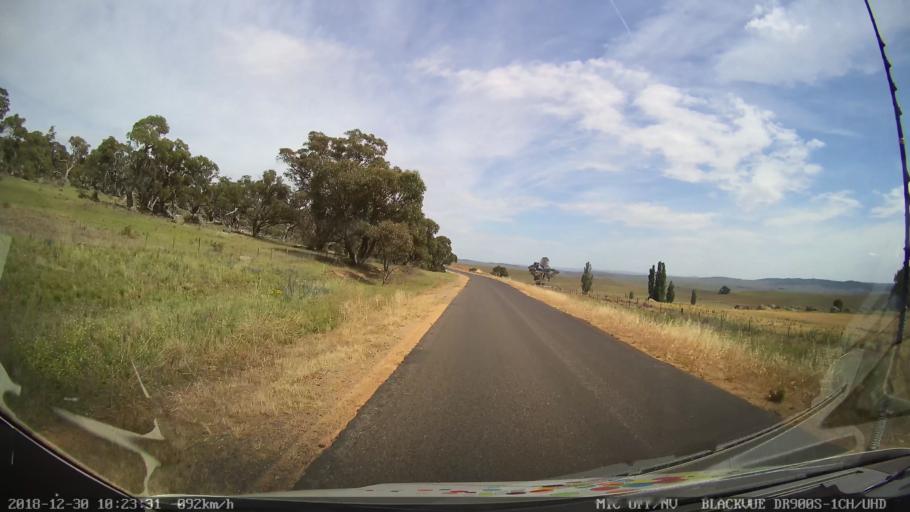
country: AU
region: New South Wales
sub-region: Snowy River
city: Berridale
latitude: -36.5365
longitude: 148.9817
